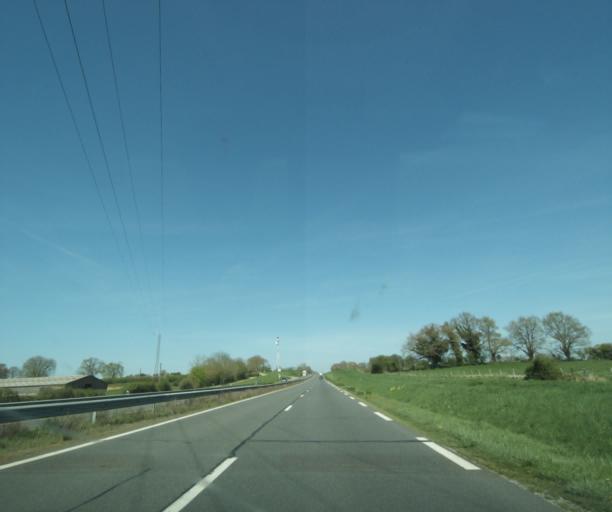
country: FR
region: Bourgogne
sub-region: Departement de la Nievre
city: Saint-Pierre-le-Moutier
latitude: 46.7766
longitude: 3.1310
